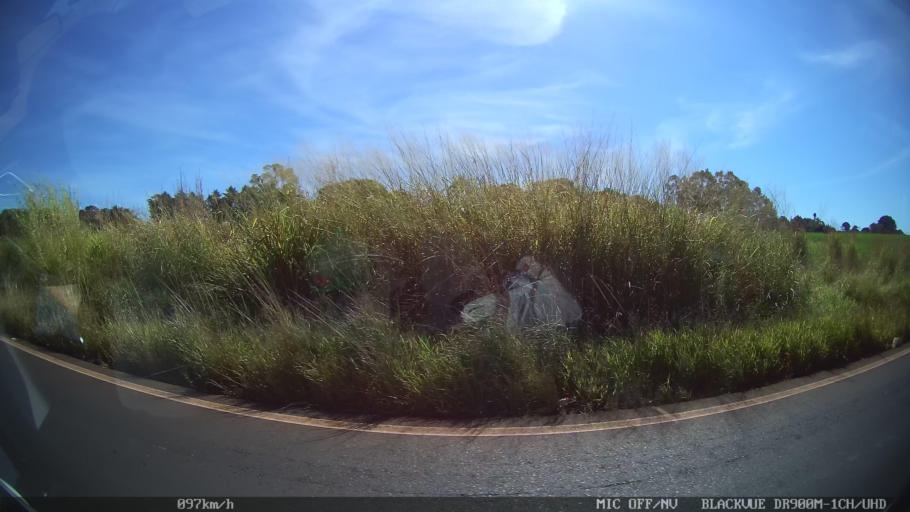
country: BR
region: Sao Paulo
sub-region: Franca
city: Franca
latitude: -20.5553
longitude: -47.4954
